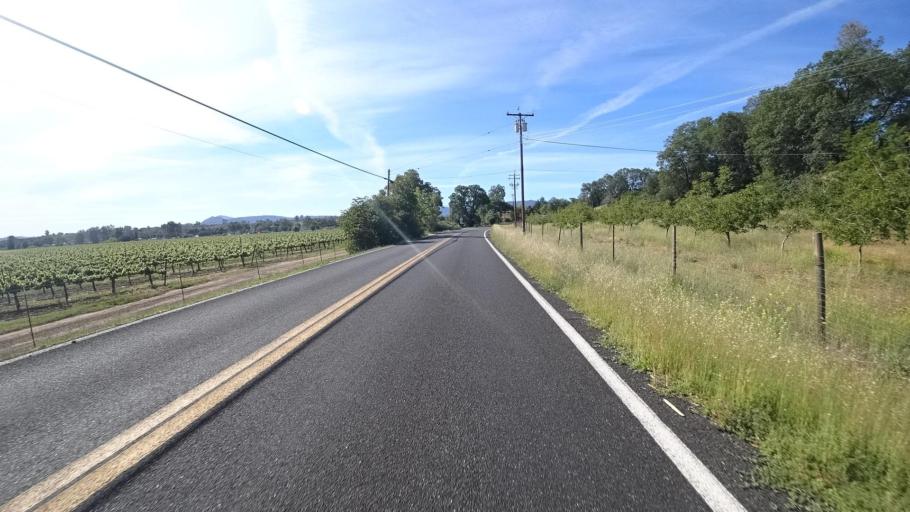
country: US
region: California
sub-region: Lake County
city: Kelseyville
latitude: 38.9592
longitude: -122.8968
